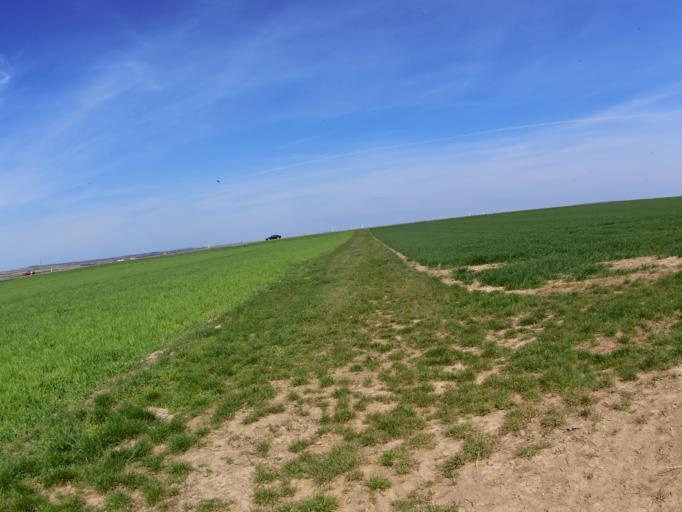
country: DE
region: Bavaria
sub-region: Regierungsbezirk Unterfranken
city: Mainstockheim
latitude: 49.7924
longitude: 10.1241
